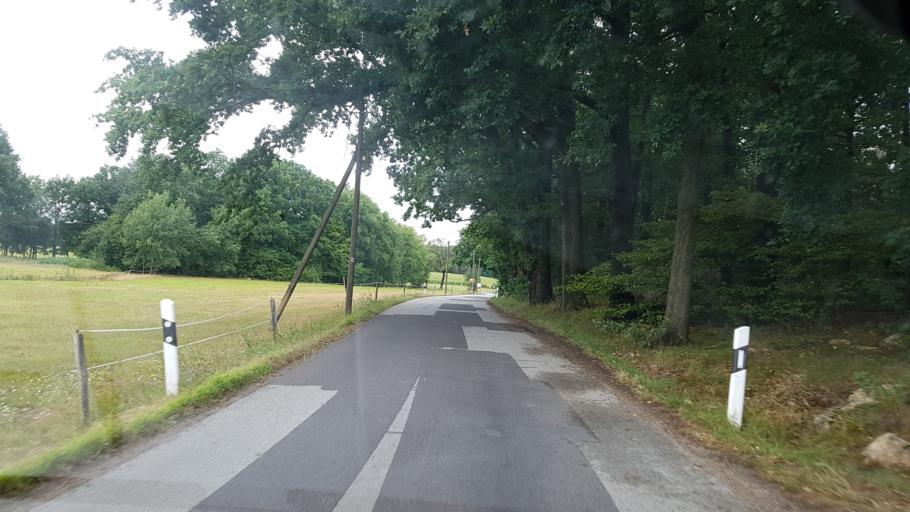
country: DE
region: Saxony
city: Konigshain
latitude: 51.2099
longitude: 14.8137
